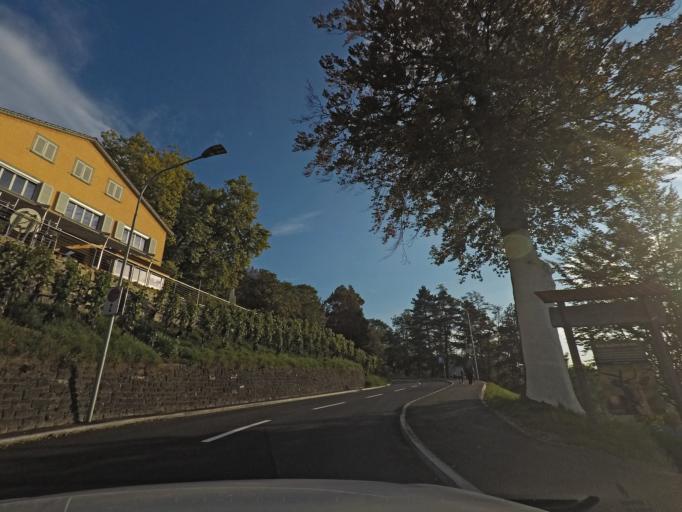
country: CH
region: Zurich
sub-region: Bezirk Zuerich
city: Zuerich (Kreis 5) / Escher-Wyss
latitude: 47.3998
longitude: 8.5157
